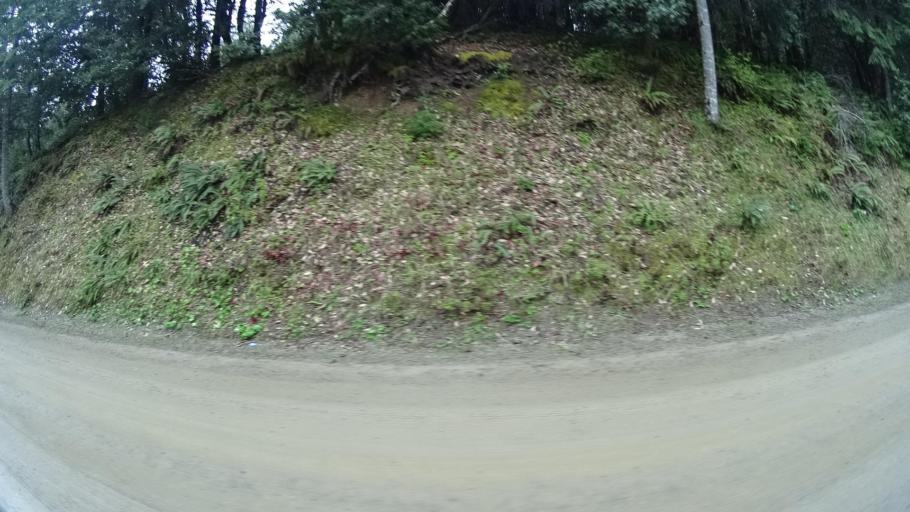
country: US
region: California
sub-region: Humboldt County
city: Westhaven-Moonstone
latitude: 41.1400
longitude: -123.8591
